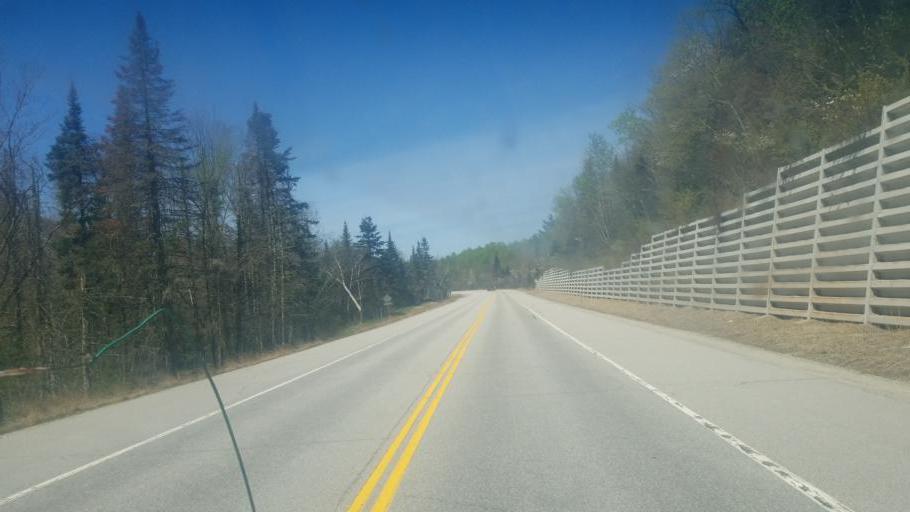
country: US
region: New Hampshire
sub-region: Grafton County
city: Deerfield
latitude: 44.2656
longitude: -71.4992
